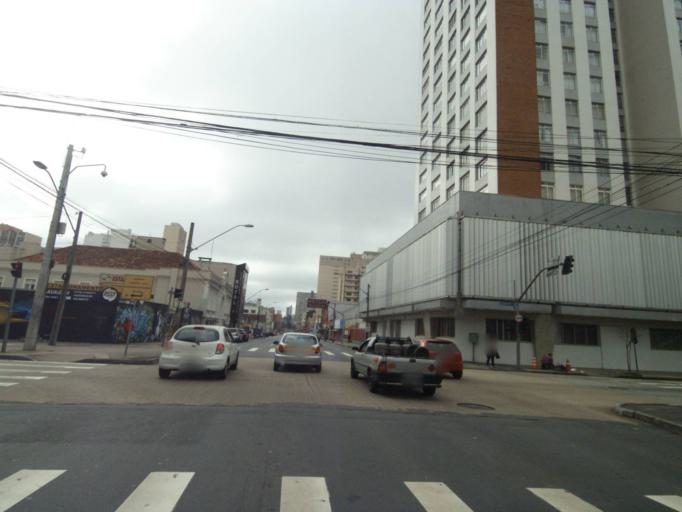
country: BR
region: Parana
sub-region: Curitiba
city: Curitiba
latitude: -25.4349
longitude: -49.2689
